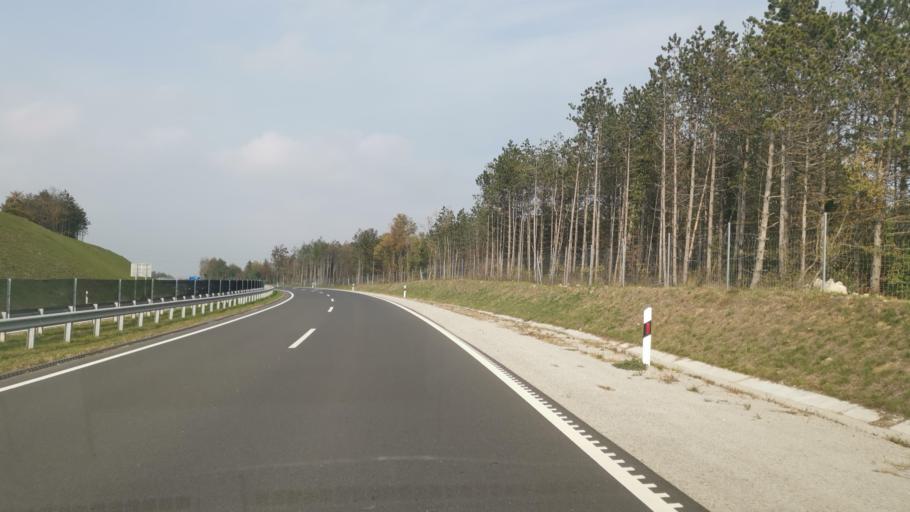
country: HU
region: Gyor-Moson-Sopron
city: Sopron
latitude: 47.6711
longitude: 16.6305
